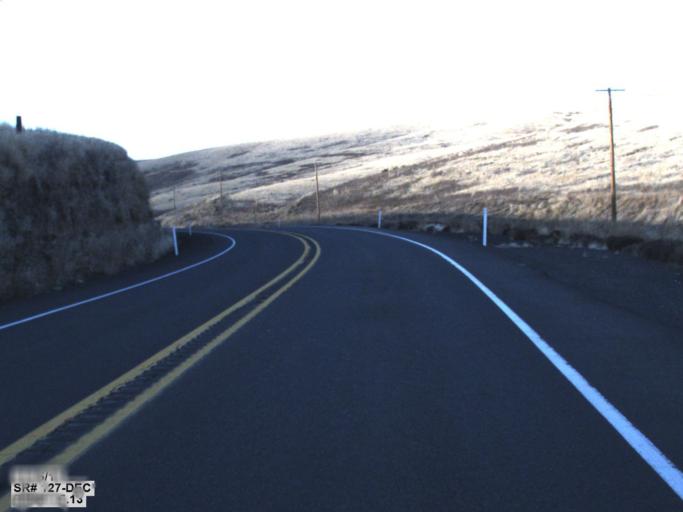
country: US
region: Washington
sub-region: Garfield County
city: Pomeroy
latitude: 46.6866
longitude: -117.8030
